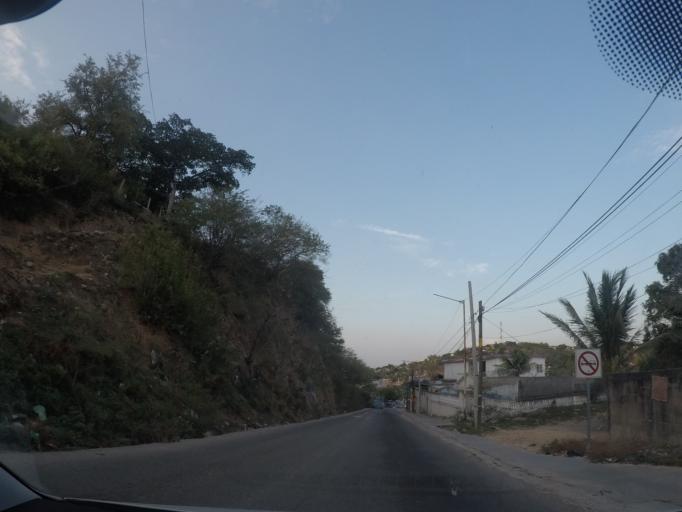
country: MX
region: Oaxaca
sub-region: Salina Cruz
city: Salina Cruz
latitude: 16.1941
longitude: -95.2053
